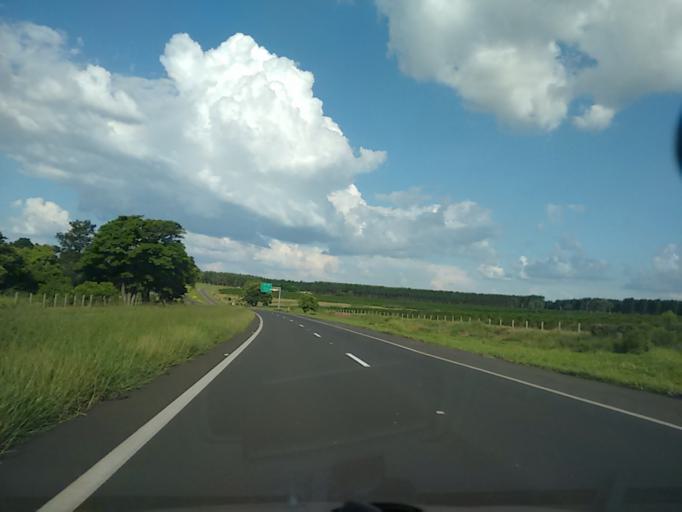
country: BR
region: Sao Paulo
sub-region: Duartina
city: Duartina
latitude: -22.3307
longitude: -49.4584
